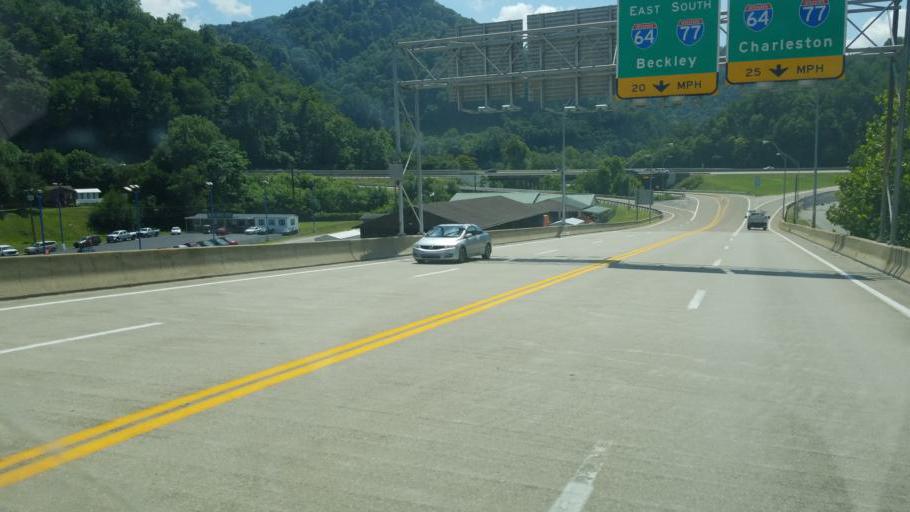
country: US
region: West Virginia
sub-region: Kanawha County
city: Chesapeake
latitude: 38.1948
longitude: -81.4979
